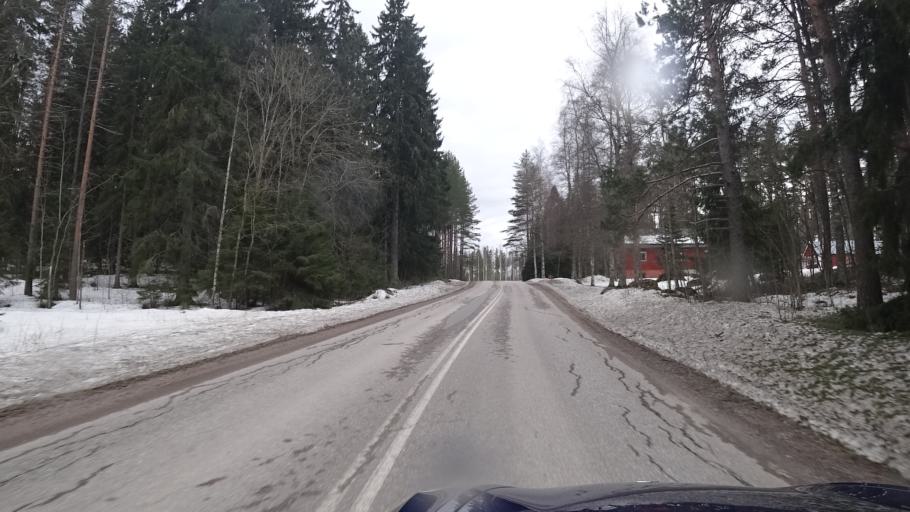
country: FI
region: Paijanne Tavastia
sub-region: Lahti
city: Nastola
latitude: 60.8834
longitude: 26.0040
